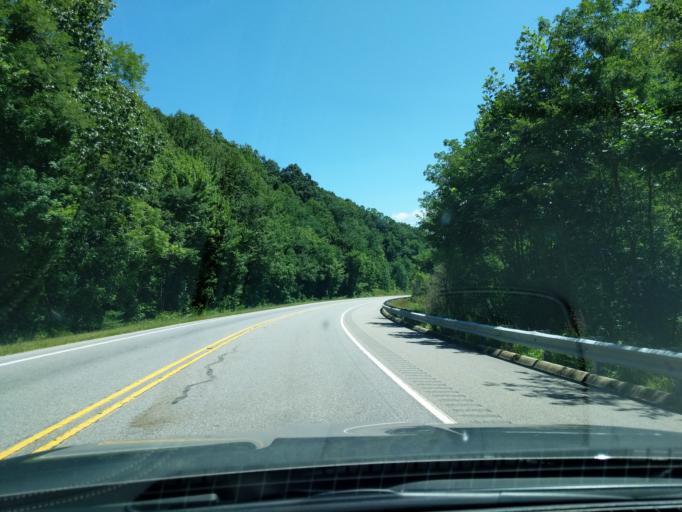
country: US
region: North Carolina
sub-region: Macon County
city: Franklin
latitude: 35.1300
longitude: -83.5279
